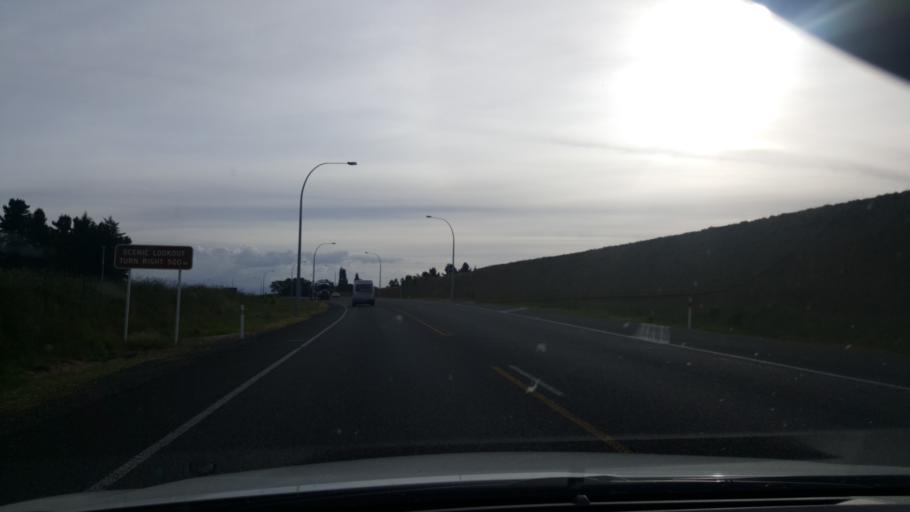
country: NZ
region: Waikato
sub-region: Taupo District
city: Taupo
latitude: -38.7349
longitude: 176.0768
